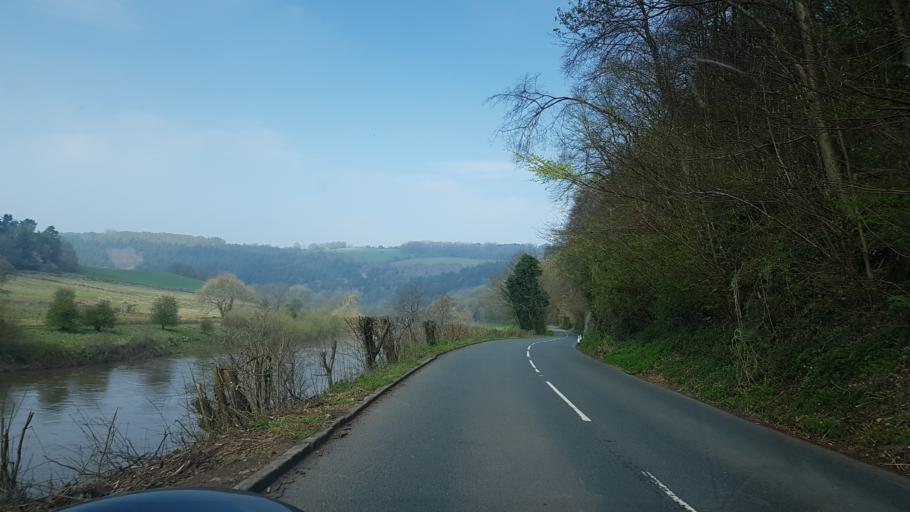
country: GB
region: Wales
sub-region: Monmouthshire
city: Tintern
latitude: 51.7467
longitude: -2.6659
